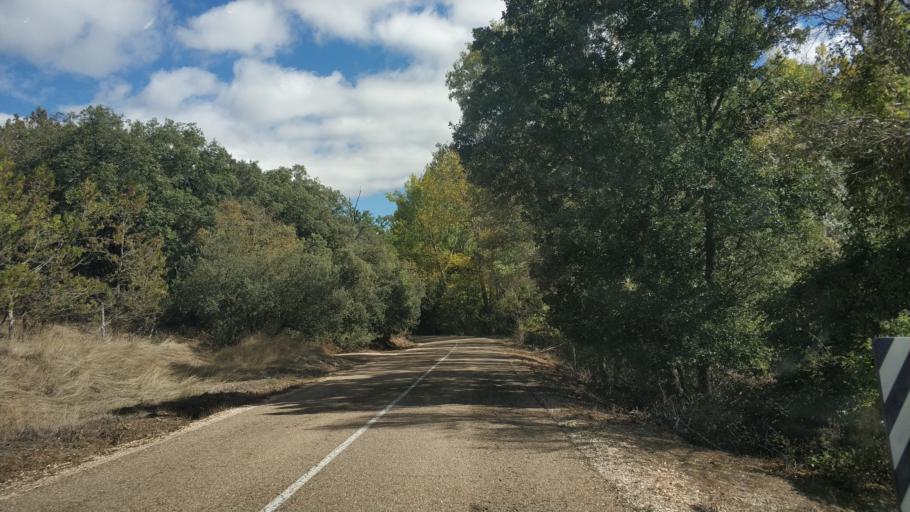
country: ES
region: Castille and Leon
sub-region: Provincia de Burgos
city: Hortiguela
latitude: 42.0473
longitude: -3.4613
